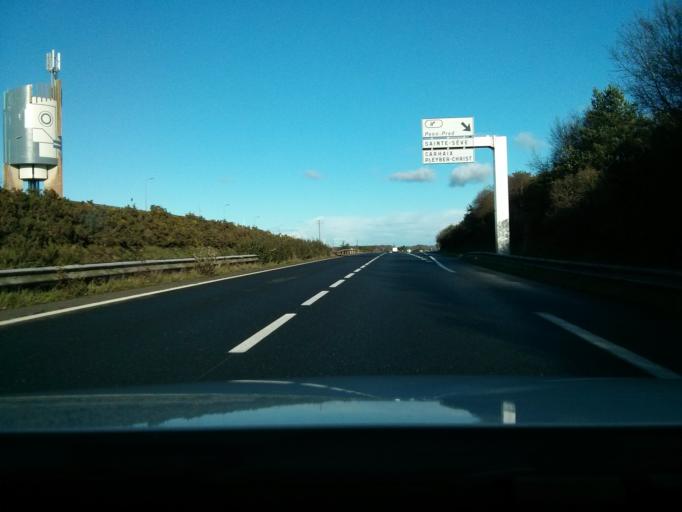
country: FR
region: Brittany
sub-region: Departement du Finistere
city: Taule
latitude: 48.5503
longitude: -3.8847
